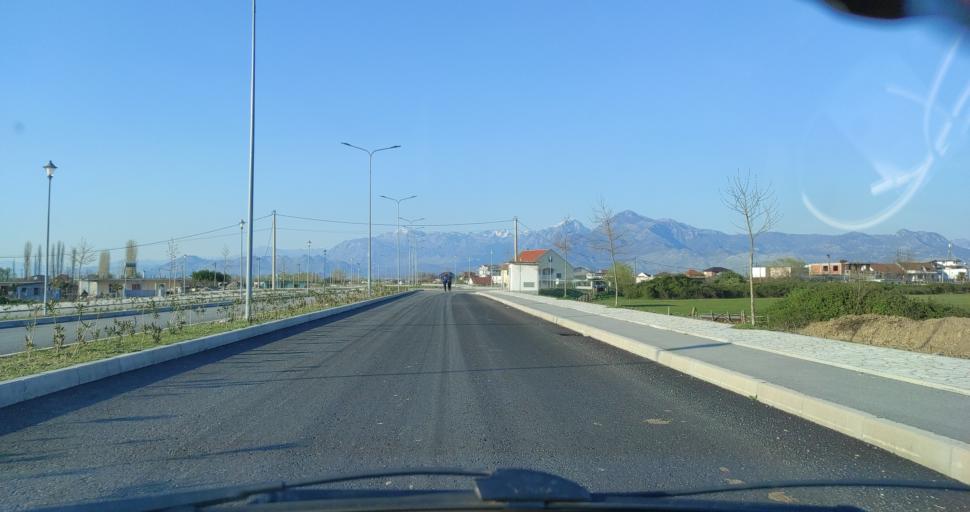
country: AL
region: Shkoder
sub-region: Rrethi i Shkodres
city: Shkoder
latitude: 42.0770
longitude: 19.4915
